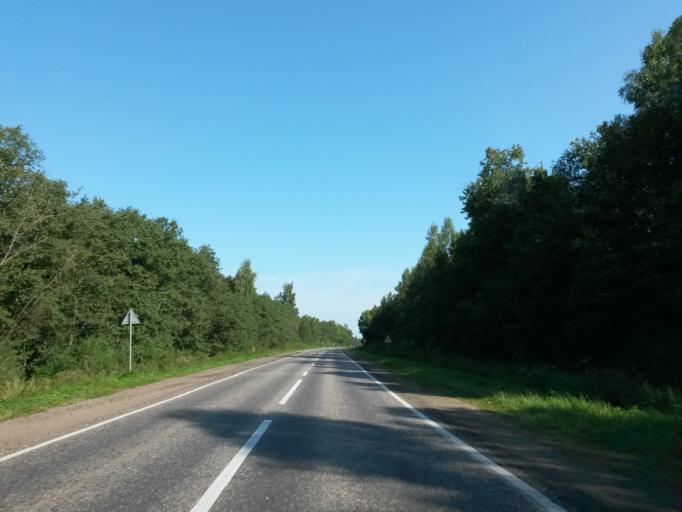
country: RU
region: Jaroslavl
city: Yaroslavl
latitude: 57.4887
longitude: 39.9020
